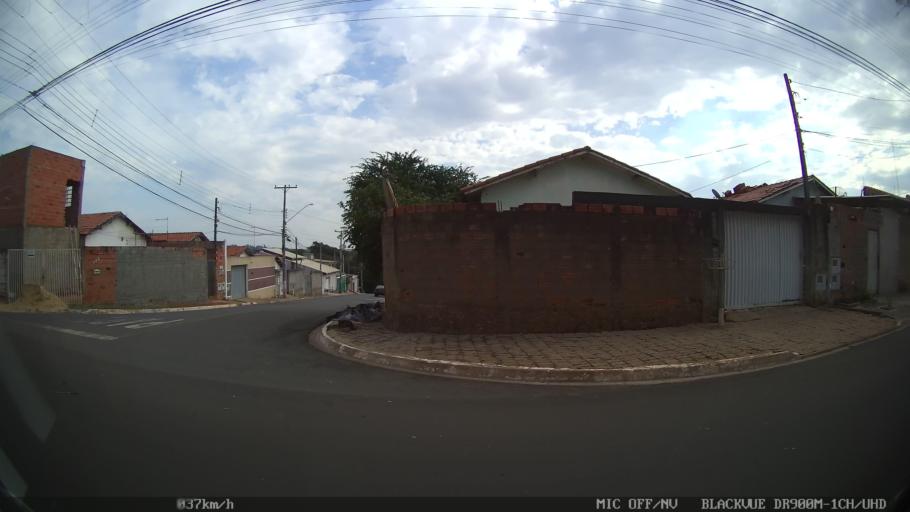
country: BR
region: Sao Paulo
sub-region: Paulinia
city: Paulinia
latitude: -22.7463
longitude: -47.1741
